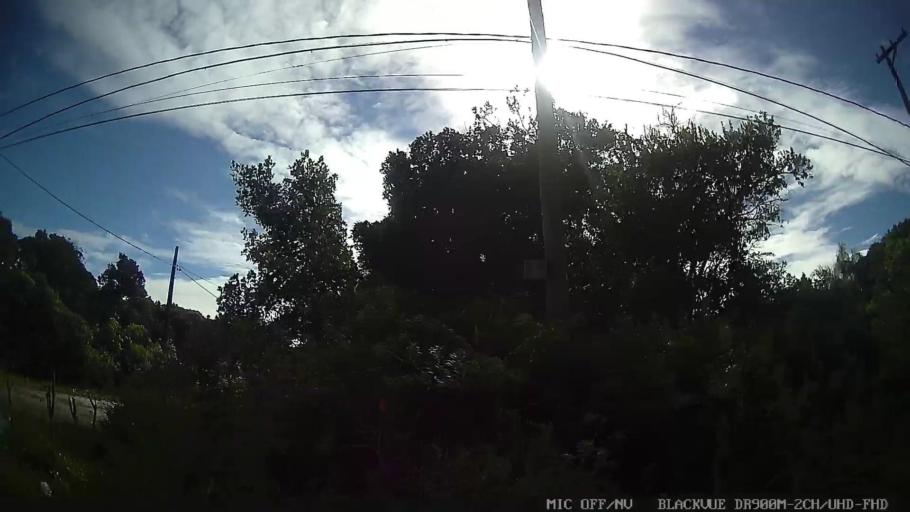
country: BR
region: Sao Paulo
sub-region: Peruibe
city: Peruibe
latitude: -24.2472
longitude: -46.9055
